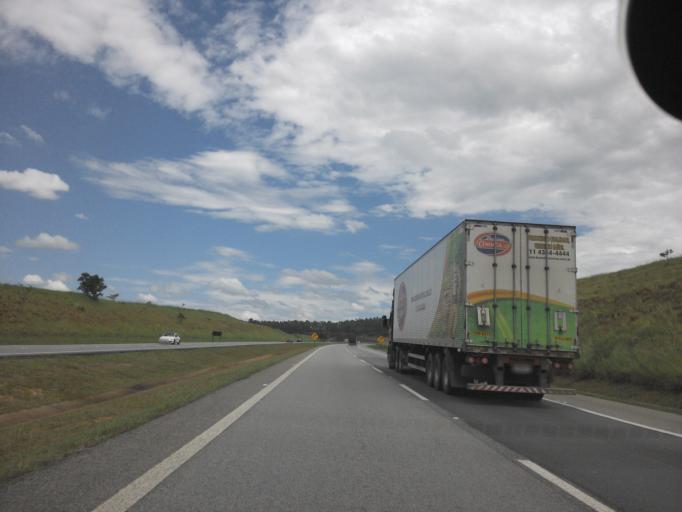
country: BR
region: Sao Paulo
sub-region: Cacapava
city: Cacapava
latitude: -23.1279
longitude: -45.6565
